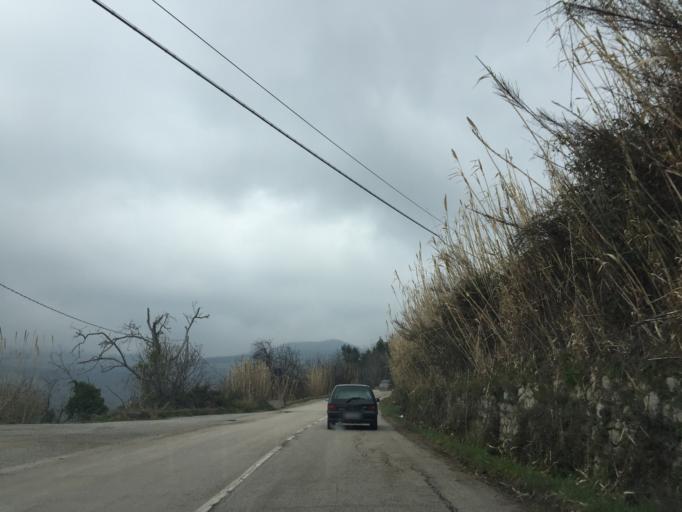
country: IT
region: Apulia
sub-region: Provincia di Foggia
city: Bovino
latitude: 41.2549
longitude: 15.3492
